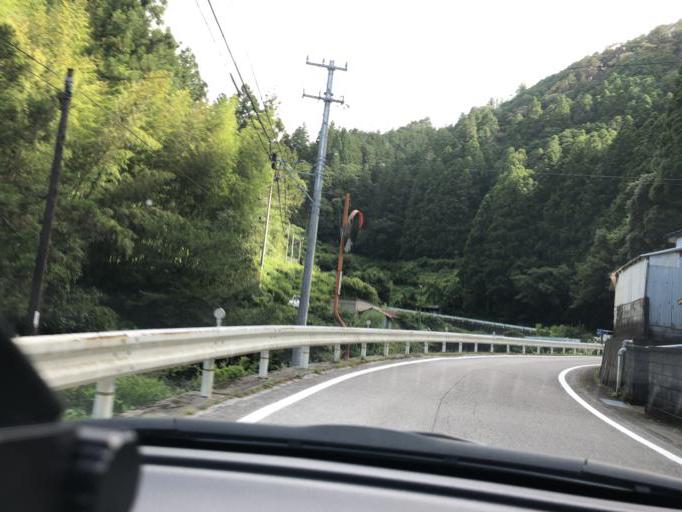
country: JP
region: Kochi
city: Kochi-shi
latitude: 33.6170
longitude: 133.4970
